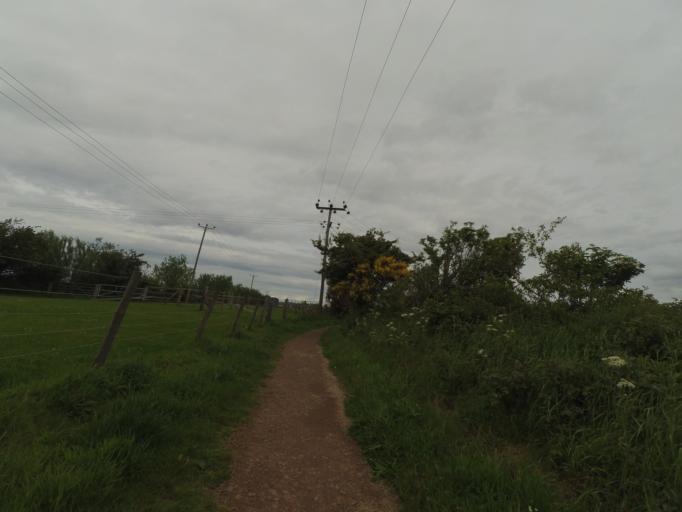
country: GB
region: Scotland
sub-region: East Lothian
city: Macmerry
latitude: 55.9372
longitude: -2.9120
